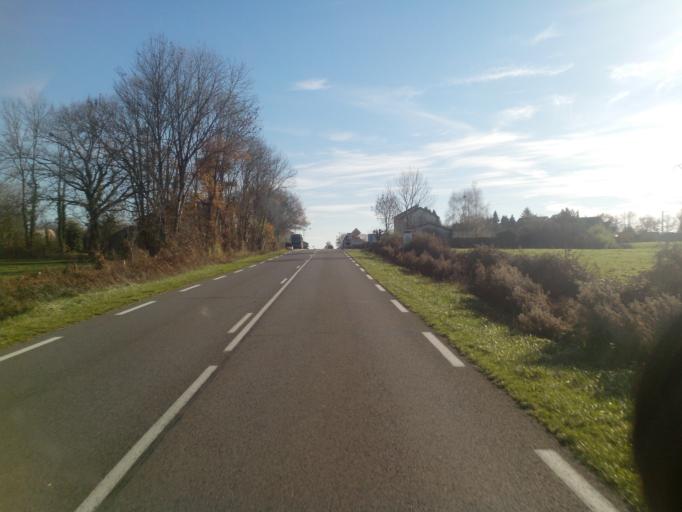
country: FR
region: Limousin
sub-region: Departement de la Haute-Vienne
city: Bussiere-Poitevine
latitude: 46.1711
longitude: 0.9507
